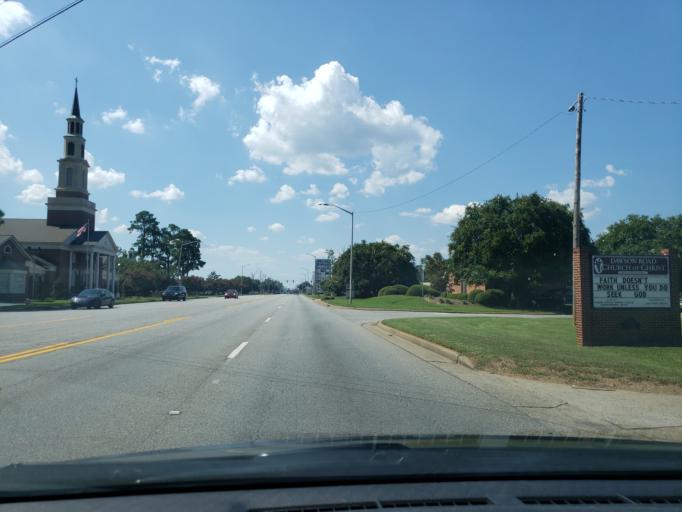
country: US
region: Georgia
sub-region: Dougherty County
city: Albany
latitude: 31.6014
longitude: -84.2022
